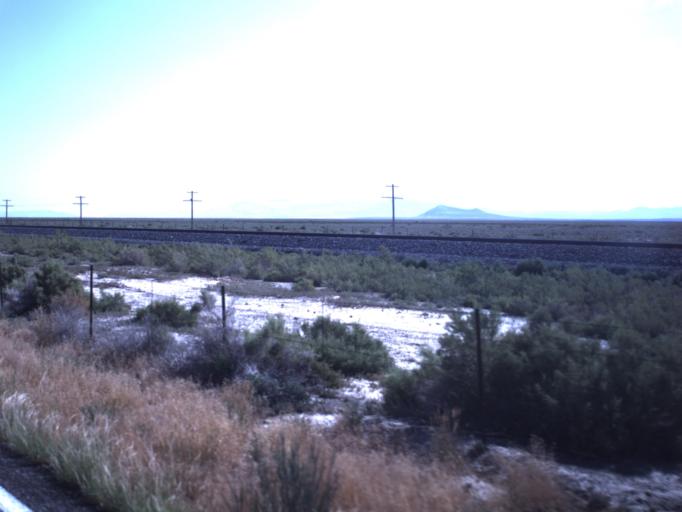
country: US
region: Utah
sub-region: Millard County
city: Delta
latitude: 39.0348
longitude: -112.7737
